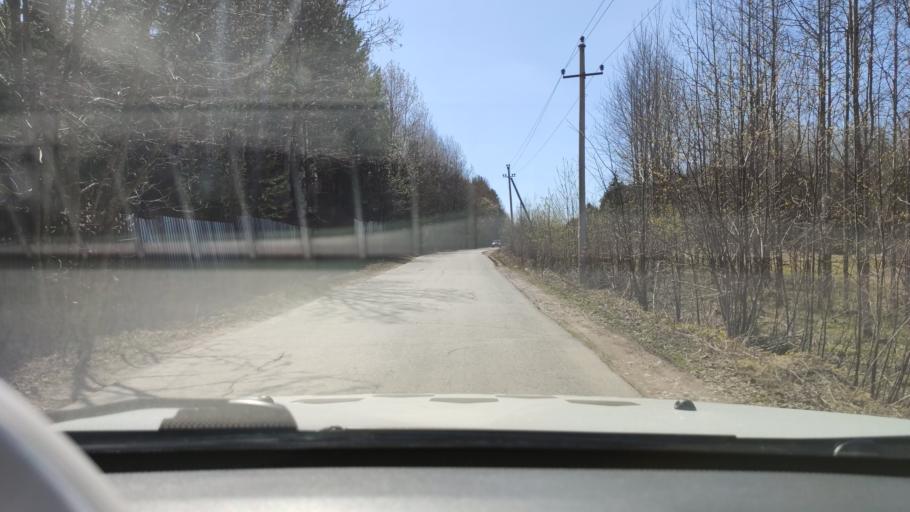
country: RU
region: Perm
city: Novyye Lyady
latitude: 58.0447
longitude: 56.6361
